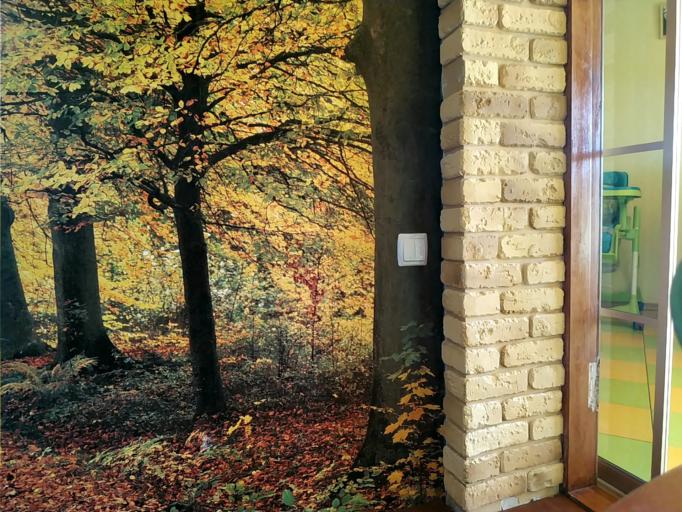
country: RU
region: Moskovskaya
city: Krasnoarmeysk
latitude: 56.0692
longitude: 38.1398
